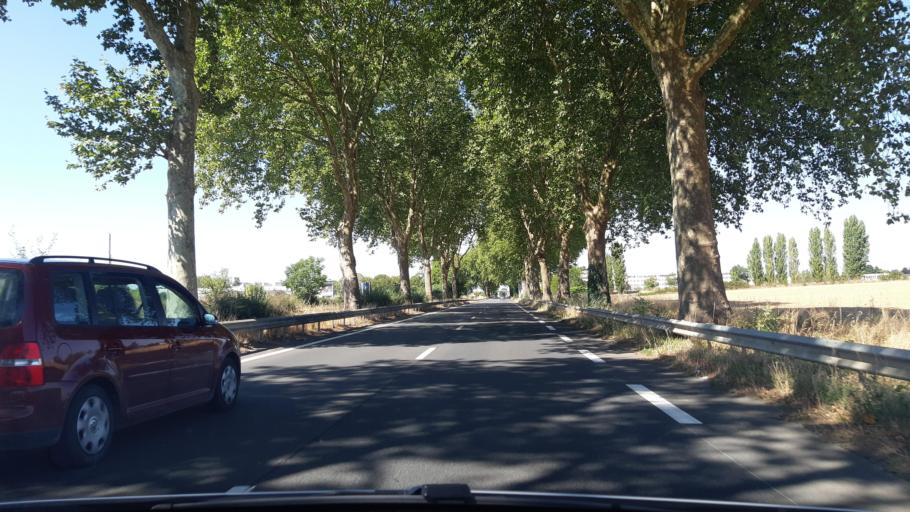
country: FR
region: Poitou-Charentes
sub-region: Departement des Deux-Sevres
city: Chauray
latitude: 46.3456
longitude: -0.3672
